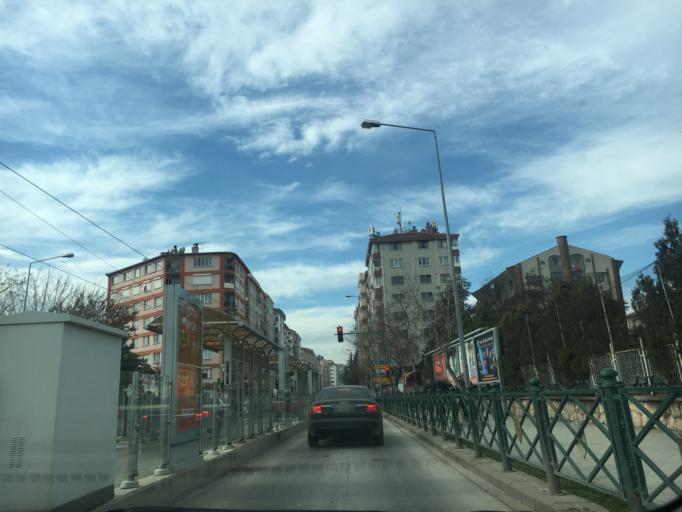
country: TR
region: Eskisehir
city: Eskisehir
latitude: 39.7697
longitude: 30.5134
